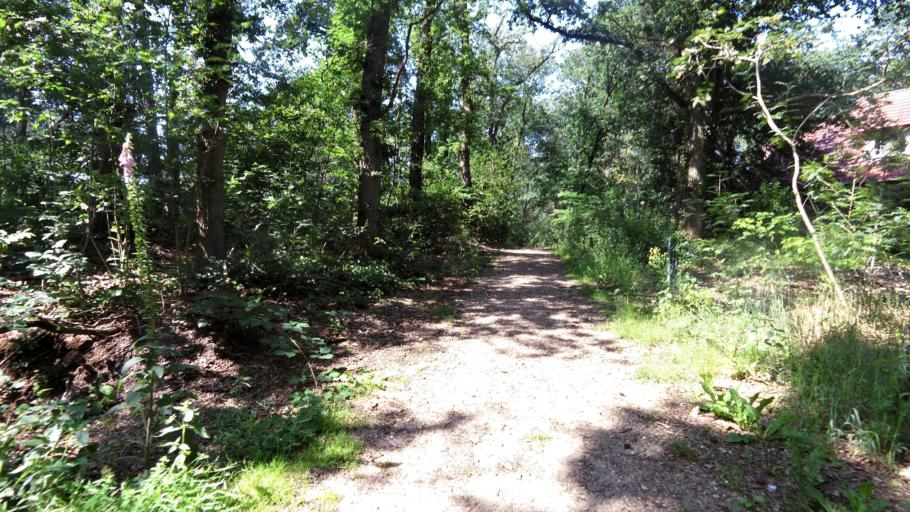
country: NL
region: Gelderland
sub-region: Gemeente Arnhem
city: Hoogkamp
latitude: 52.0185
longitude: 5.8710
